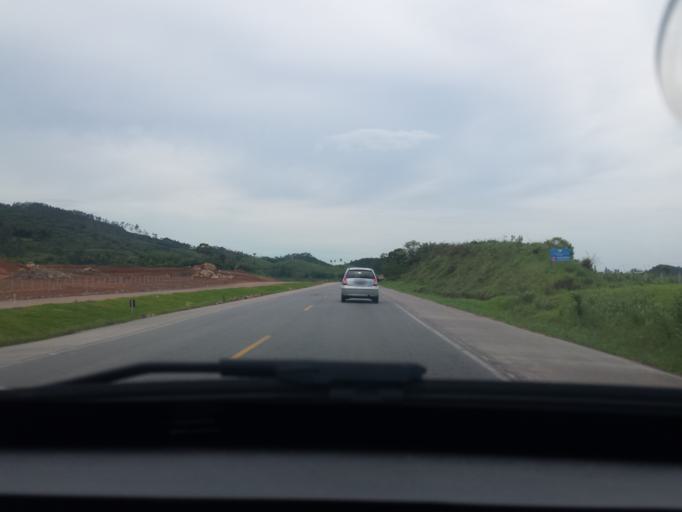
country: BR
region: Santa Catarina
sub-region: Gaspar
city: Gaspar
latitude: -26.8840
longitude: -48.8666
